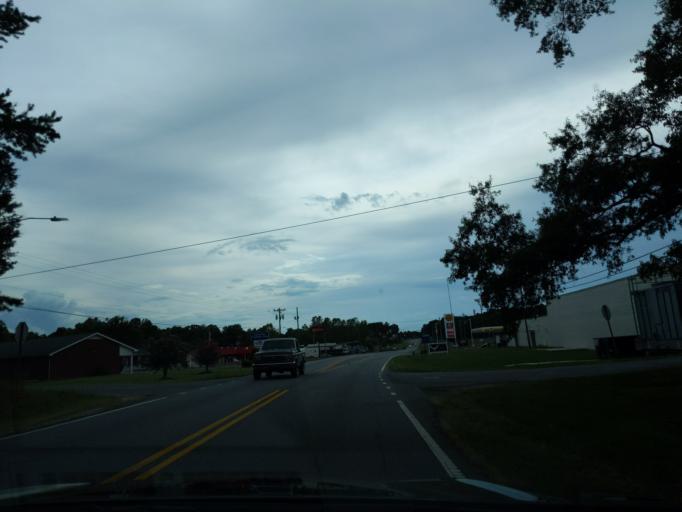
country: US
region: North Carolina
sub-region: Cabarrus County
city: Mount Pleasant
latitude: 35.4110
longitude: -80.4332
